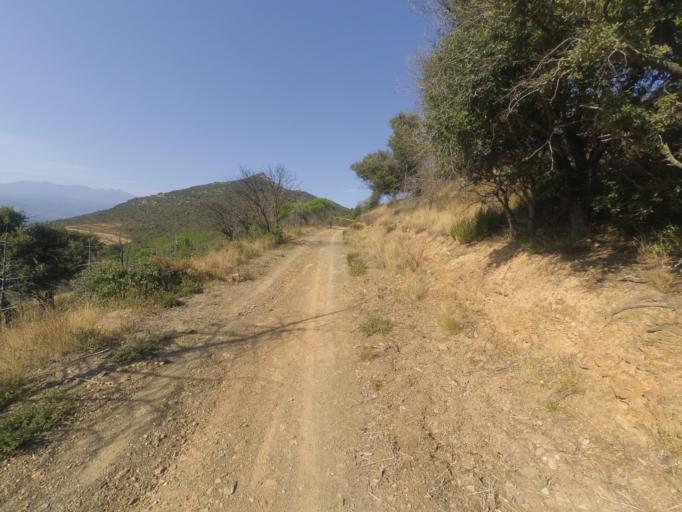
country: FR
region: Languedoc-Roussillon
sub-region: Departement des Pyrenees-Orientales
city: Corneilla-la-Riviere
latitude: 42.7312
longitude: 2.7113
